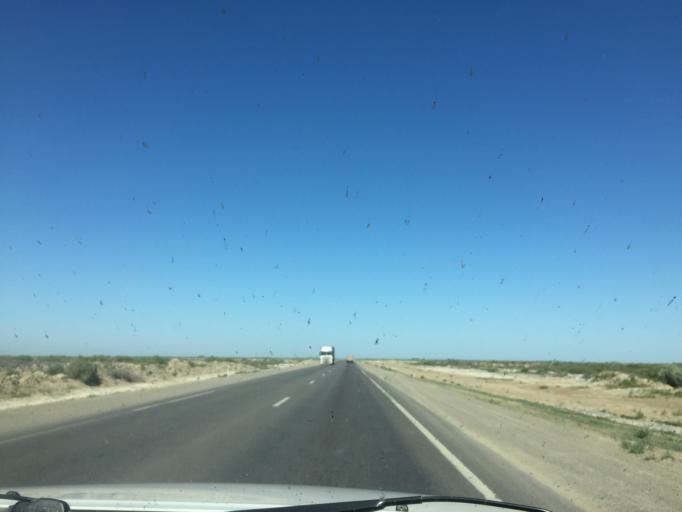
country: KZ
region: Qyzylorda
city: Terenozek
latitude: 44.8855
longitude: 65.1965
